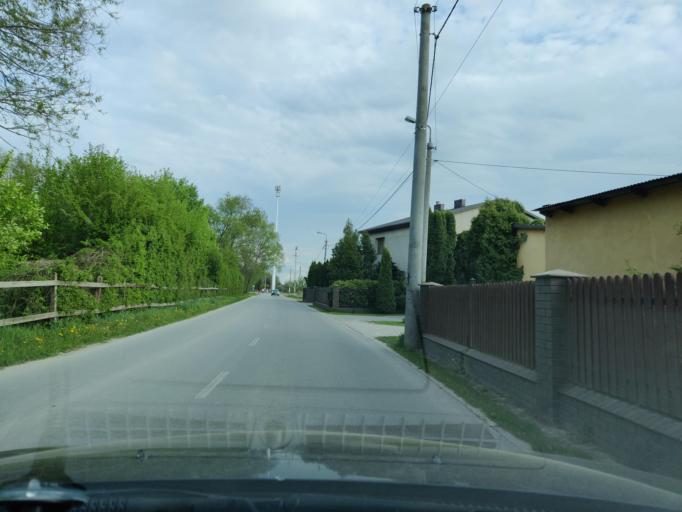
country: PL
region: Masovian Voivodeship
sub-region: Powiat piaseczynski
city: Konstancin-Jeziorna
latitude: 52.1278
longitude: 21.1386
